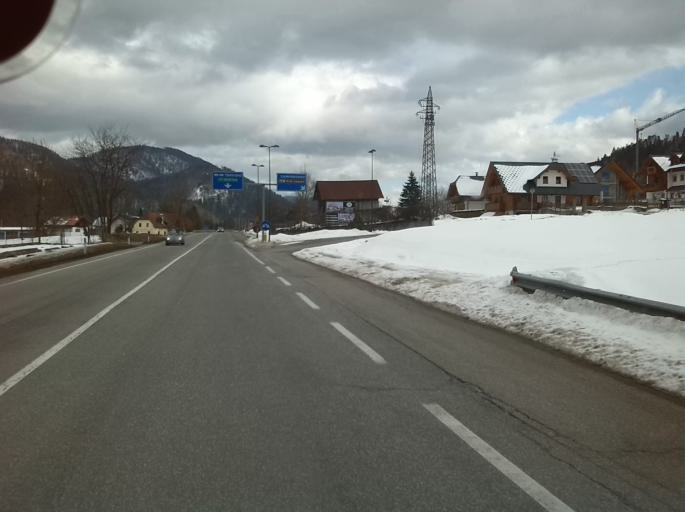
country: IT
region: Friuli Venezia Giulia
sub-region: Provincia di Udine
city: Tarvisio
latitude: 46.5074
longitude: 13.5382
